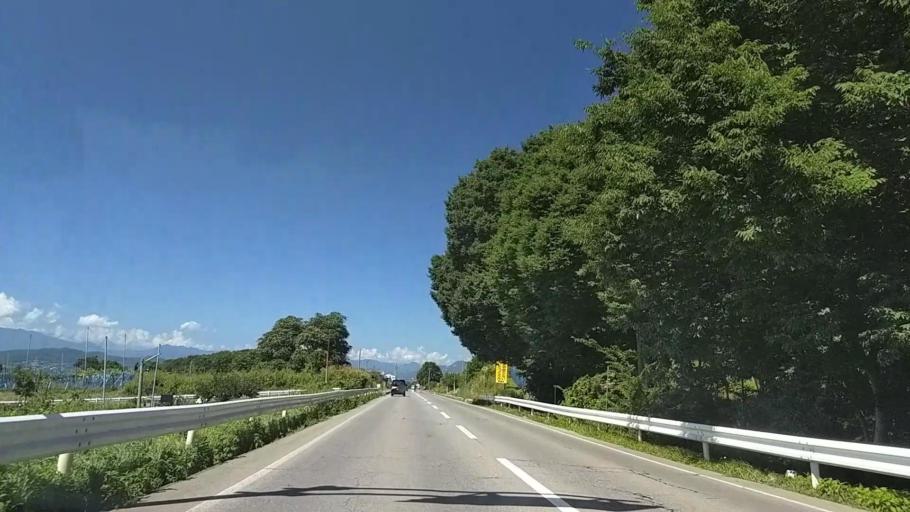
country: JP
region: Nagano
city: Komoro
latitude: 36.3594
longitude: 138.3649
